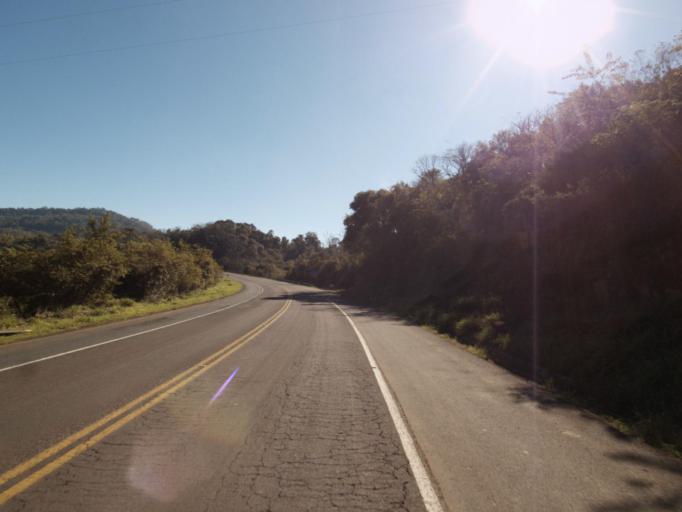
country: BR
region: Rio Grande do Sul
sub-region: Frederico Westphalen
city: Frederico Westphalen
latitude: -27.0009
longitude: -53.2259
